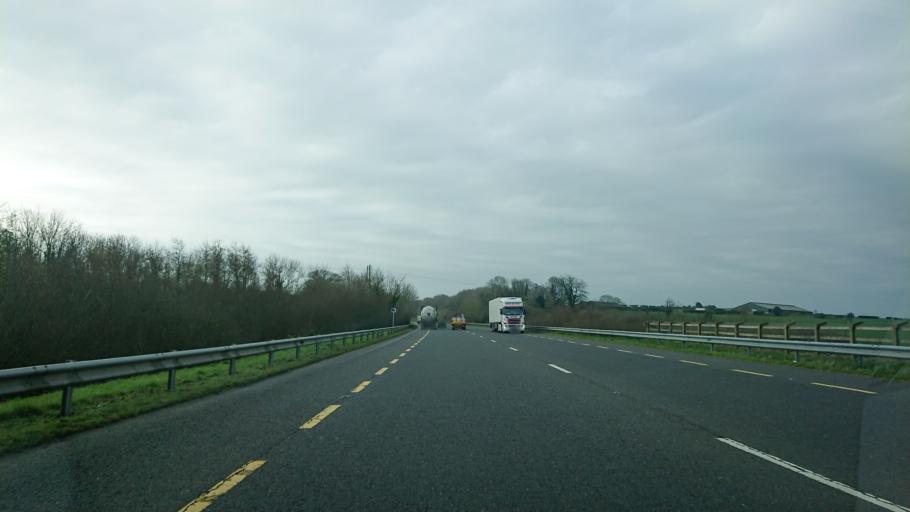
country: IE
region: Munster
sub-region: County Cork
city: Youghal
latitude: 51.9721
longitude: -7.8739
